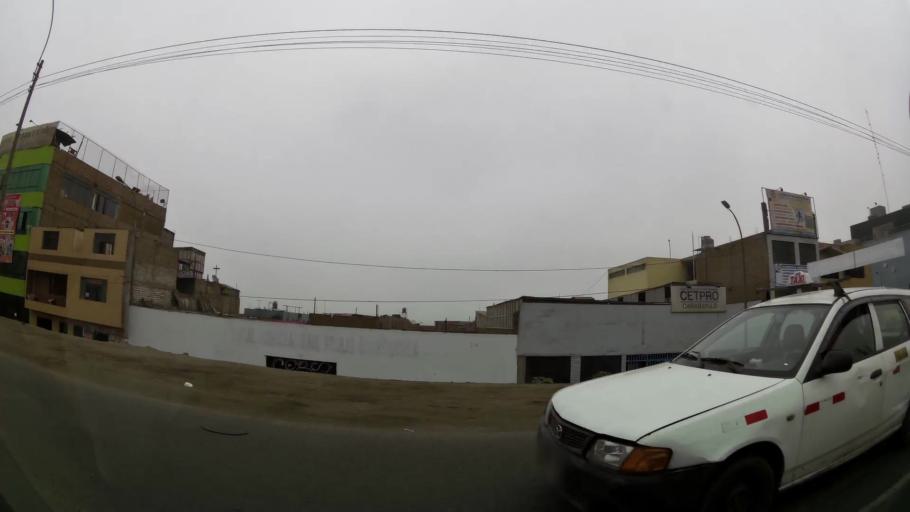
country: PE
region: Lima
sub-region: Lima
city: Urb. Santo Domingo
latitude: -11.8909
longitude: -77.0272
